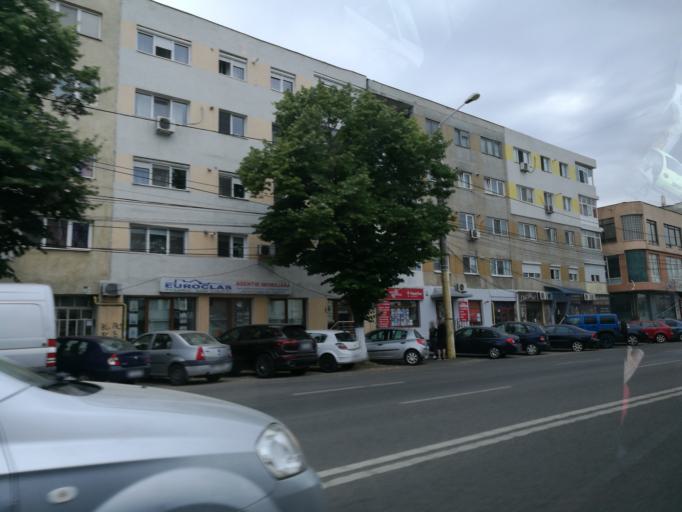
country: RO
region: Constanta
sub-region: Municipiul Constanta
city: Constanta
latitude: 44.1950
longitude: 28.6322
